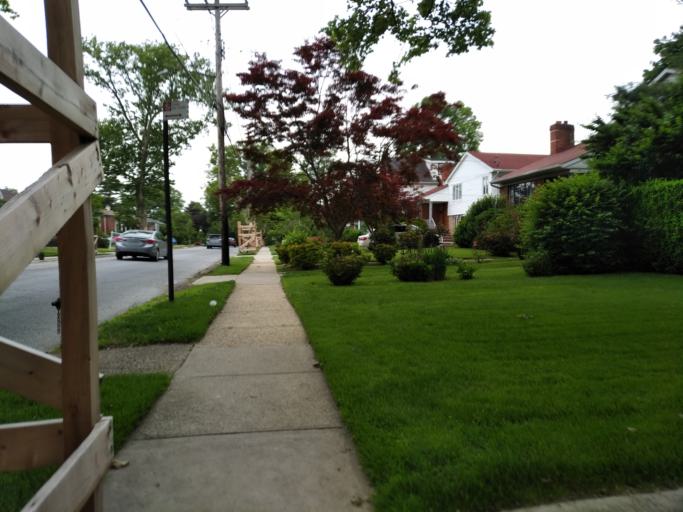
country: US
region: New York
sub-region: Nassau County
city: East Atlantic Beach
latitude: 40.7667
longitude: -73.7928
